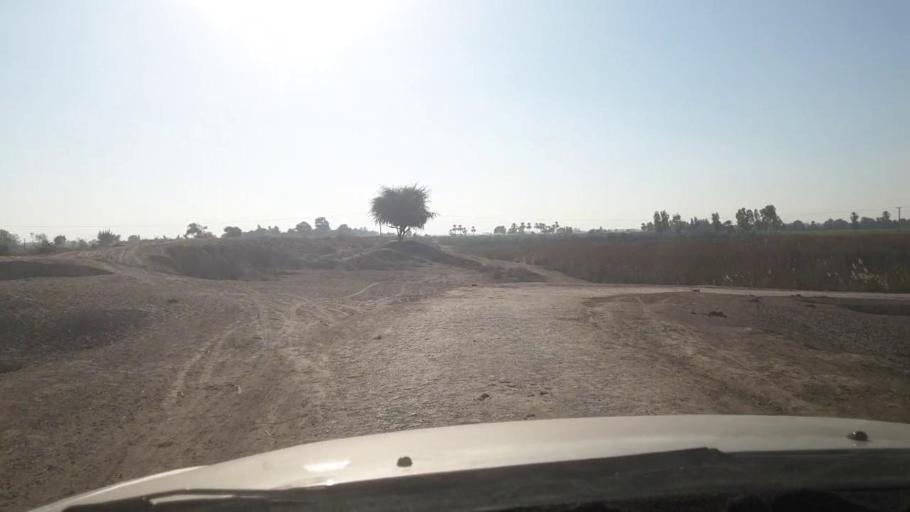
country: PK
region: Sindh
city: Ghotki
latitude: 28.0417
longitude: 69.2971
